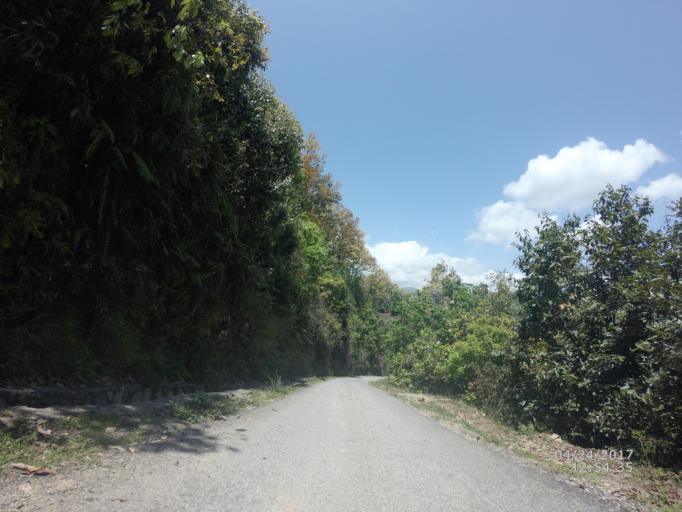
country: NP
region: Western Region
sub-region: Gandaki Zone
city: Pokhara
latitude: 28.1868
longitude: 84.0901
